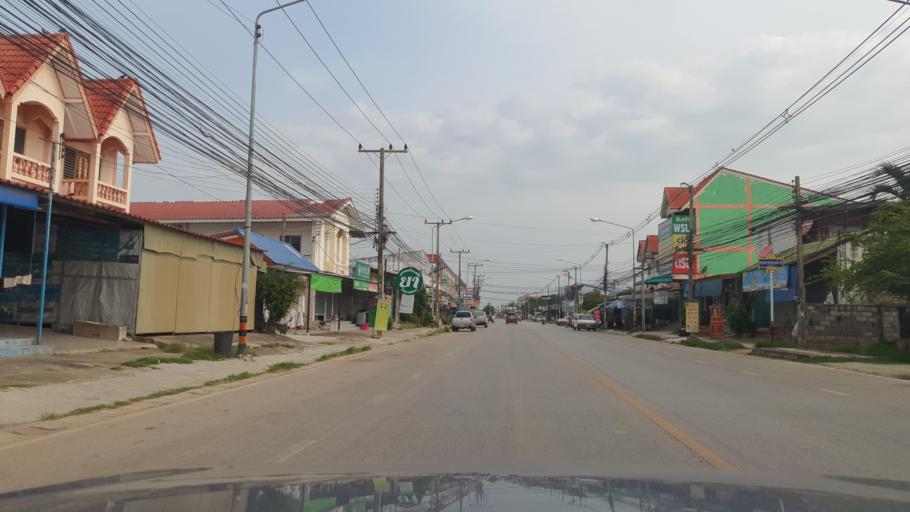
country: TH
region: Phitsanulok
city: Phitsanulok
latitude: 16.8539
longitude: 100.2540
